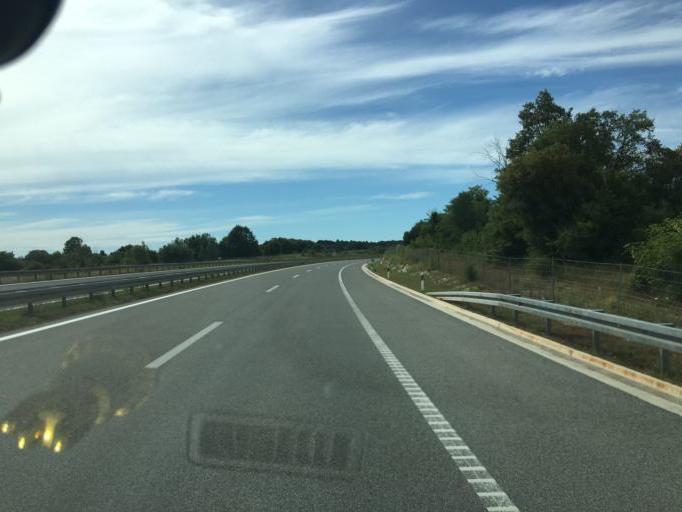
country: HR
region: Istarska
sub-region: Grad Rovinj
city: Rovinj
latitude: 45.1261
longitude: 13.7769
